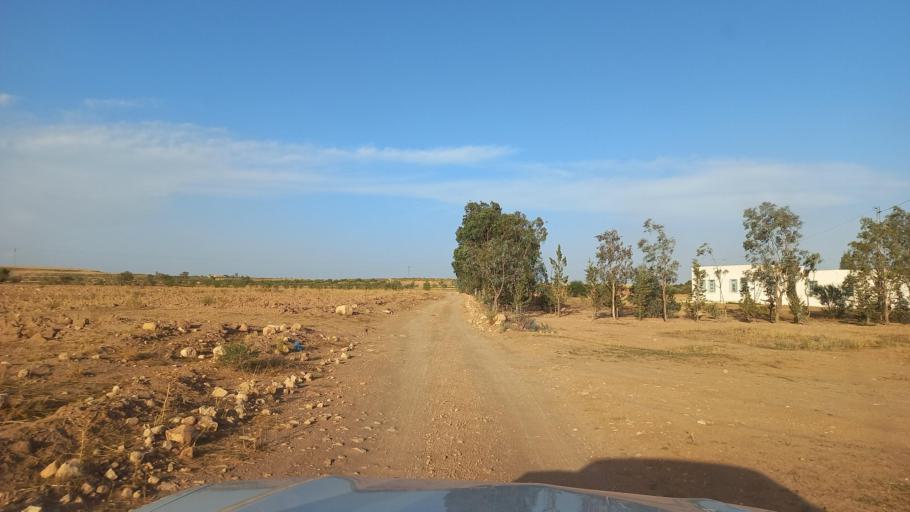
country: TN
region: Al Qasrayn
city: Kasserine
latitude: 35.2563
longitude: 8.9110
